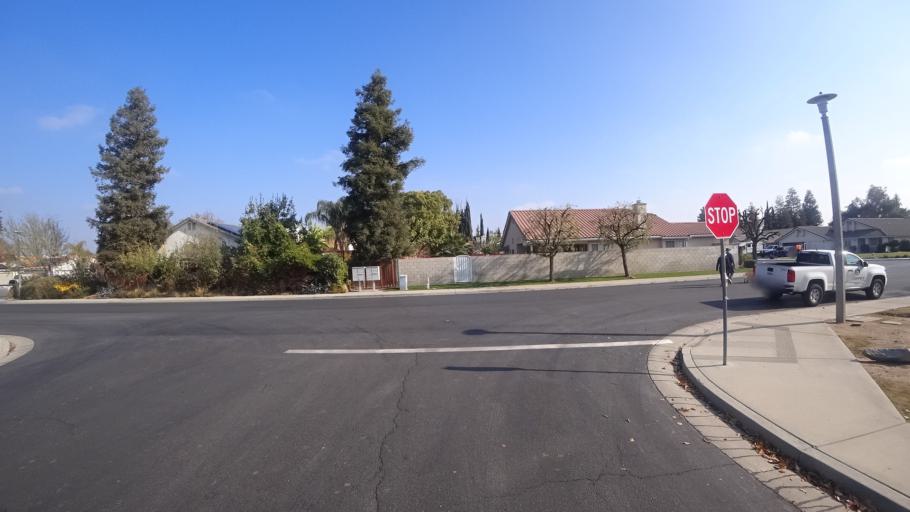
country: US
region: California
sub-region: Kern County
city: Greenacres
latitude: 35.3022
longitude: -119.0865
